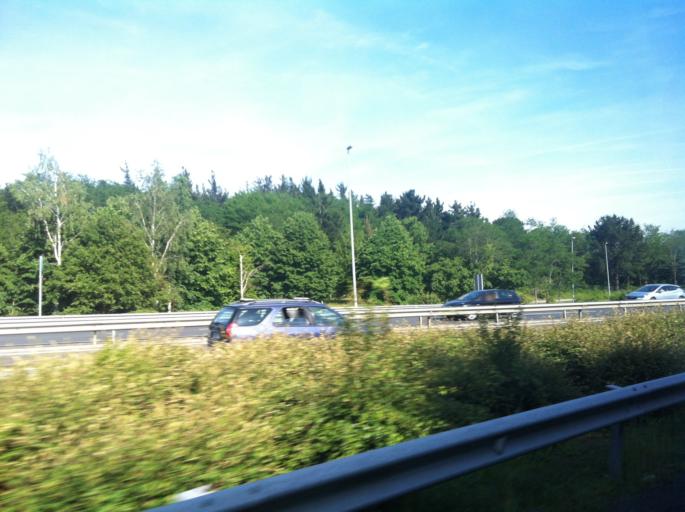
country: ES
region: Basque Country
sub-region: Bizkaia
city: Derio
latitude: 43.3069
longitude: -2.8801
